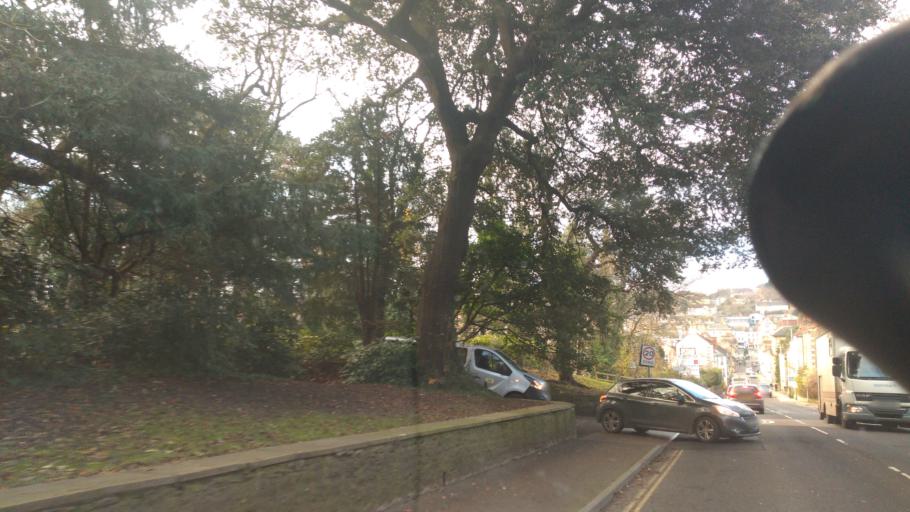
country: GB
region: England
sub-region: Somerset
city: Frome
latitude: 51.2337
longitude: -2.3176
